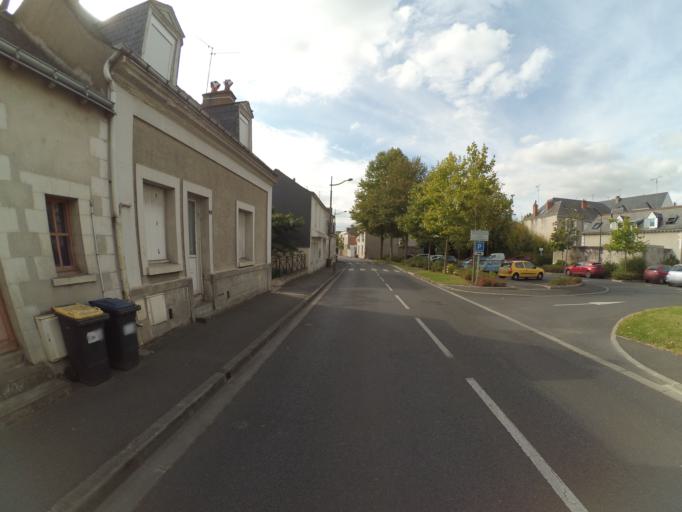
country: FR
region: Centre
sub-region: Departement d'Indre-et-Loire
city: Saint-Cyr-sur-Loire
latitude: 47.3962
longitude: 0.6591
